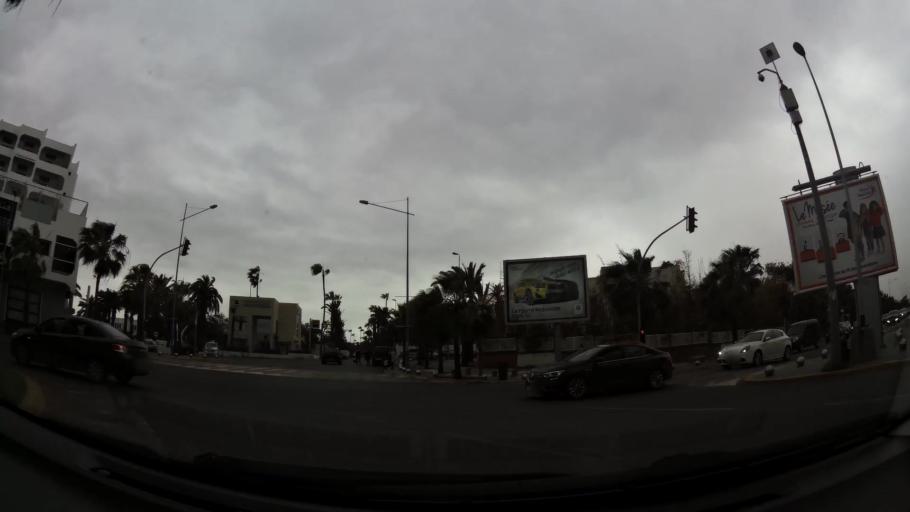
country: MA
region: Grand Casablanca
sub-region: Casablanca
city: Casablanca
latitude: 33.5915
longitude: -7.6775
